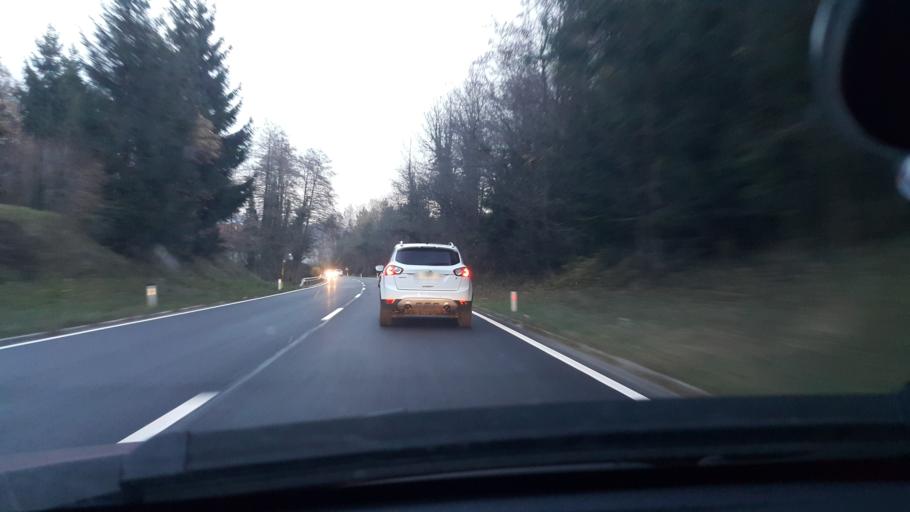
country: SI
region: Velenje
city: Velenje
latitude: 46.3464
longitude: 15.1569
